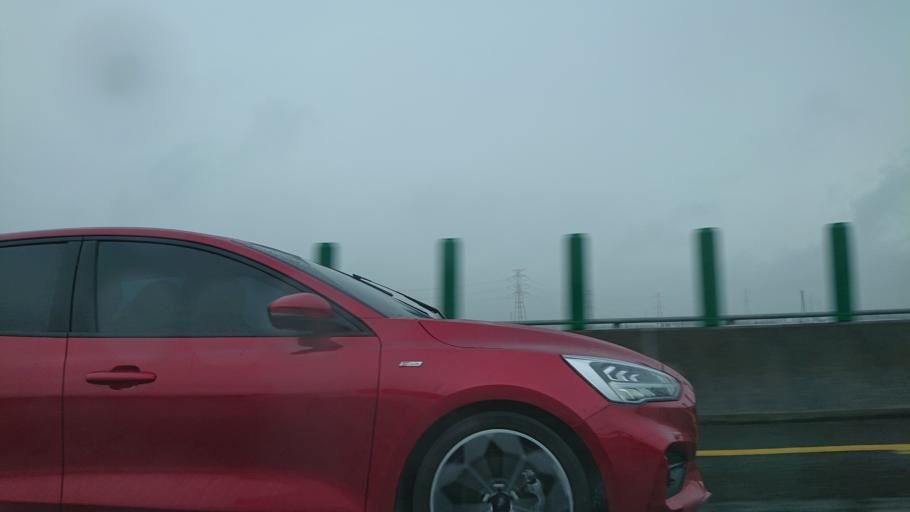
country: TW
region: Taiwan
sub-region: Yunlin
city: Douliu
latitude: 23.7721
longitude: 120.2724
